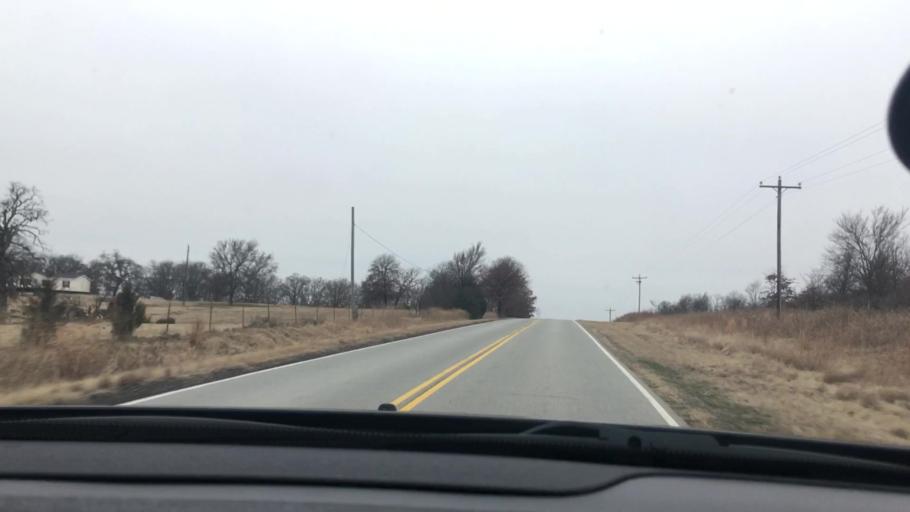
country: US
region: Oklahoma
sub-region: Coal County
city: Coalgate
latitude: 34.5055
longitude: -96.3457
